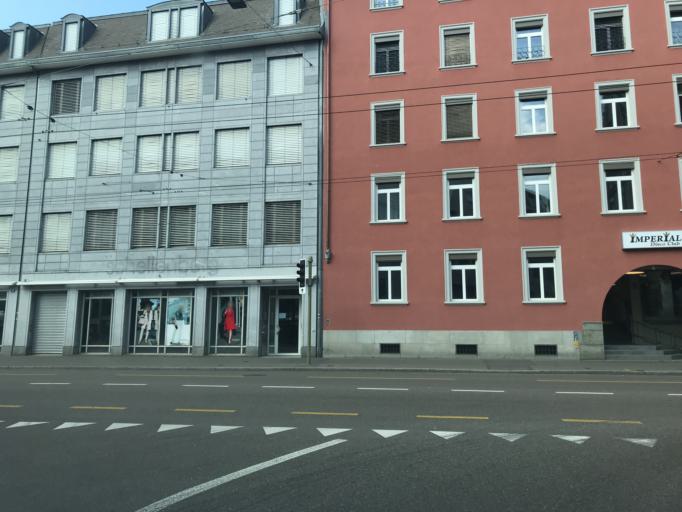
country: CH
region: Zurich
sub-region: Bezirk Winterthur
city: Winterthur
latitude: 47.4984
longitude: 8.7250
